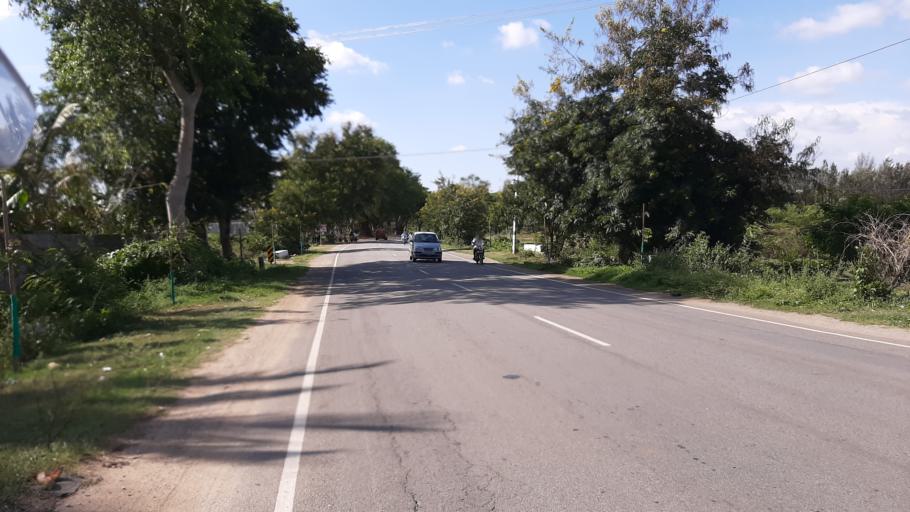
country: IN
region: Tamil Nadu
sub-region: Krishnagiri
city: Denkanikota
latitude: 12.5441
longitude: 77.7880
